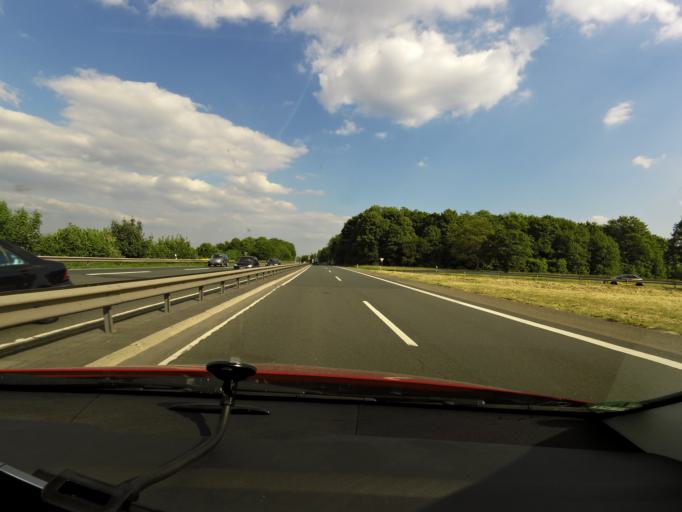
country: DE
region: Rheinland-Pfalz
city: Weissenthurm
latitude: 50.4129
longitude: 7.4385
